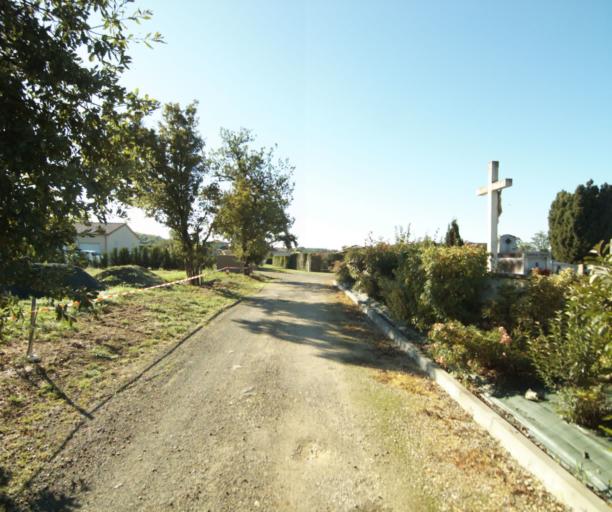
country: FR
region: Midi-Pyrenees
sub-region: Departement du Gers
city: Gondrin
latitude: 43.8390
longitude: 0.2549
